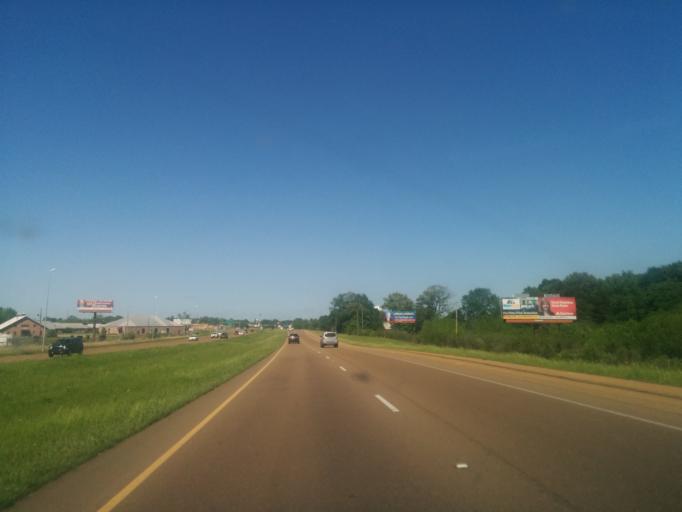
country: US
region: Mississippi
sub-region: Madison County
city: Madison
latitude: 32.5091
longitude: -90.1091
